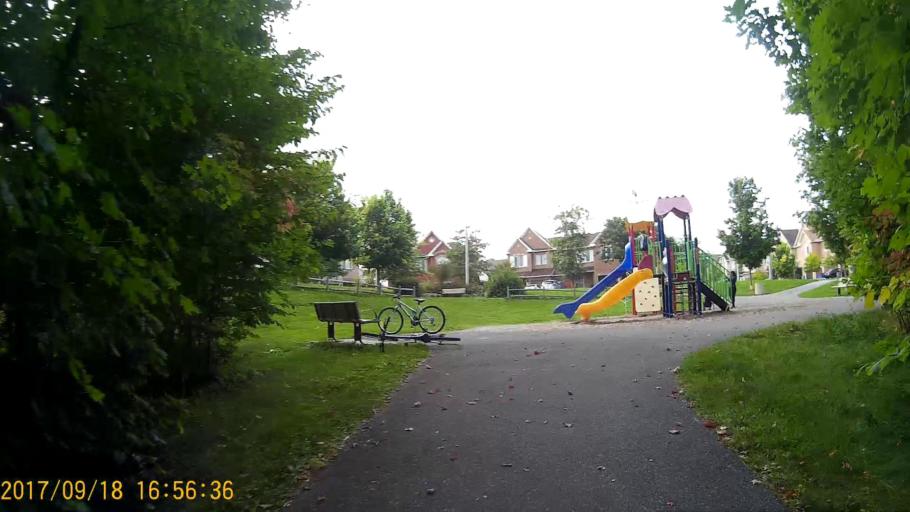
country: CA
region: Ontario
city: Bells Corners
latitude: 45.3451
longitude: -75.9406
